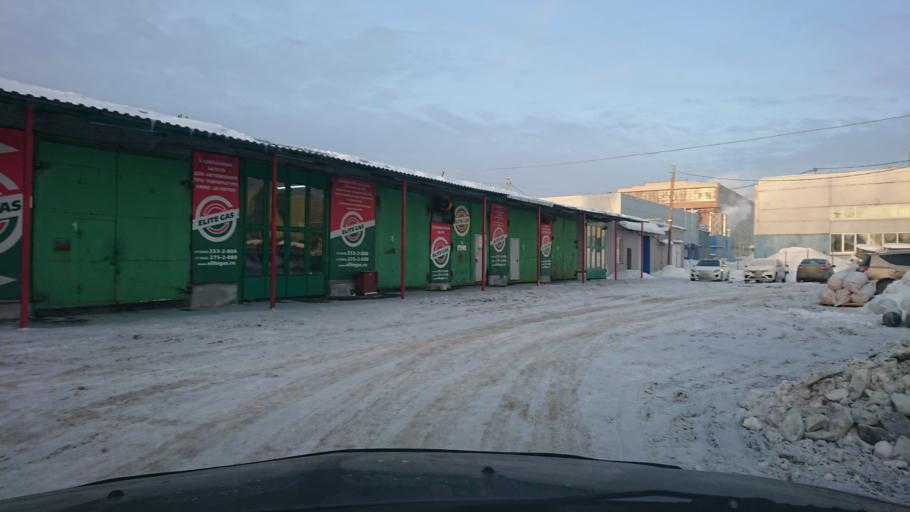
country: RU
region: Sverdlovsk
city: Yekaterinburg
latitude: 56.8727
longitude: 60.6601
